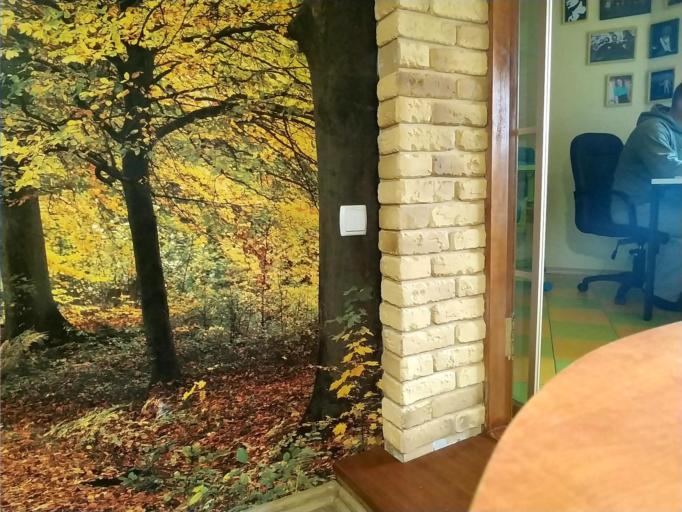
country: RU
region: Smolensk
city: Dorogobuzh
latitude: 54.9681
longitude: 33.2779
